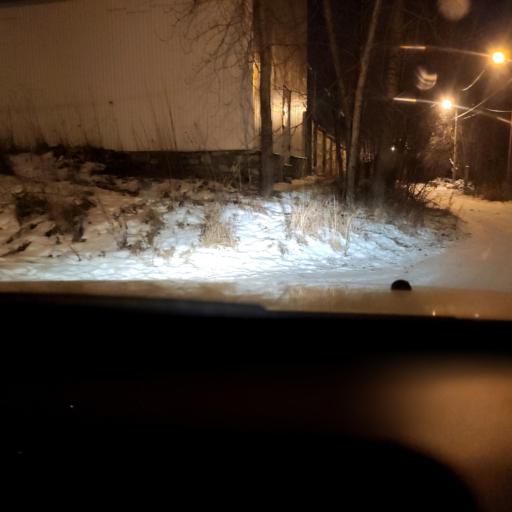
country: RU
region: Perm
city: Perm
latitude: 58.0236
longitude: 56.1751
